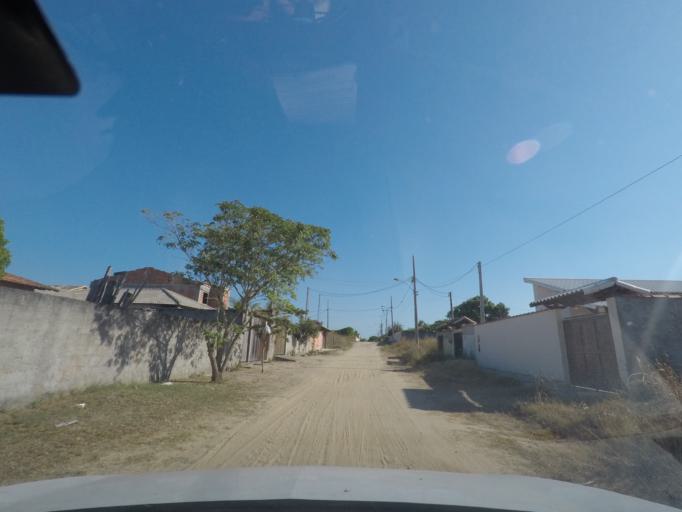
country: BR
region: Rio de Janeiro
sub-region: Marica
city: Marica
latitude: -22.9671
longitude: -42.9127
